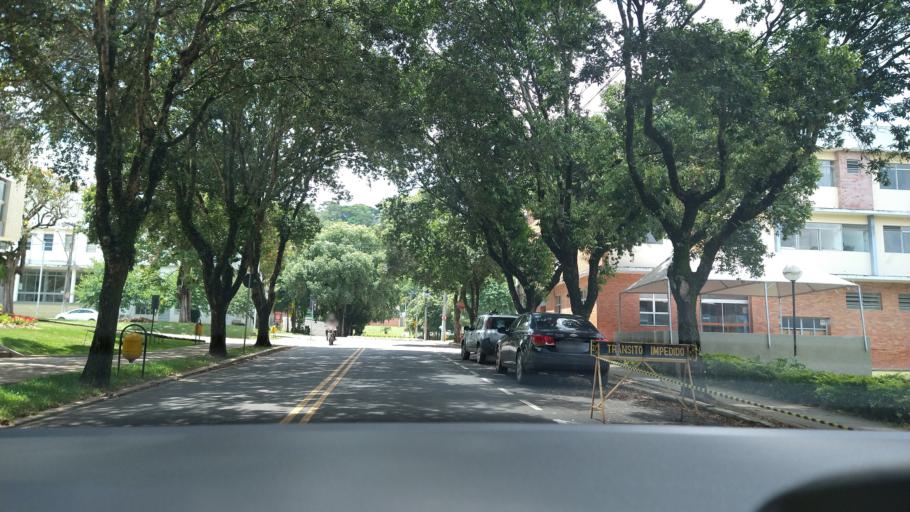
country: BR
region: Minas Gerais
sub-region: Vicosa
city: Vicosa
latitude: -20.7614
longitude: -42.8669
